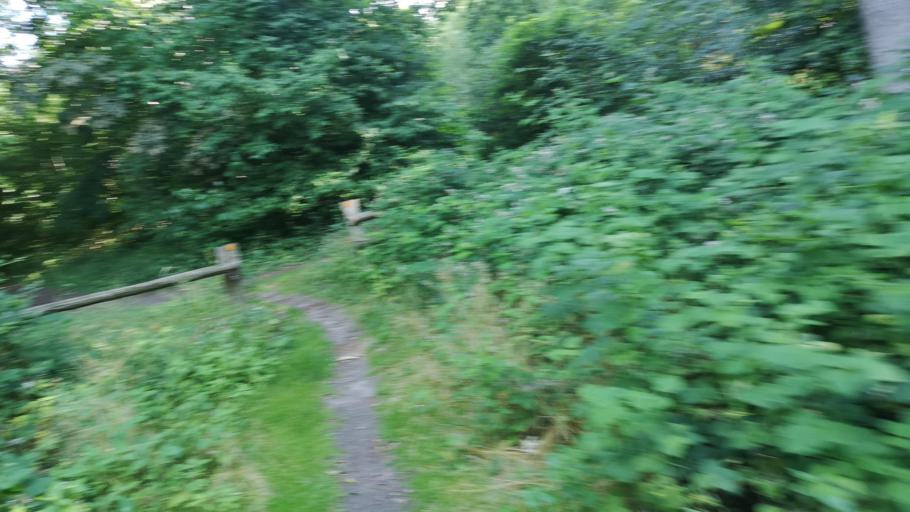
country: DE
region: Lower Saxony
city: Dahlenburg
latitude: 53.2099
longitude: 10.7190
